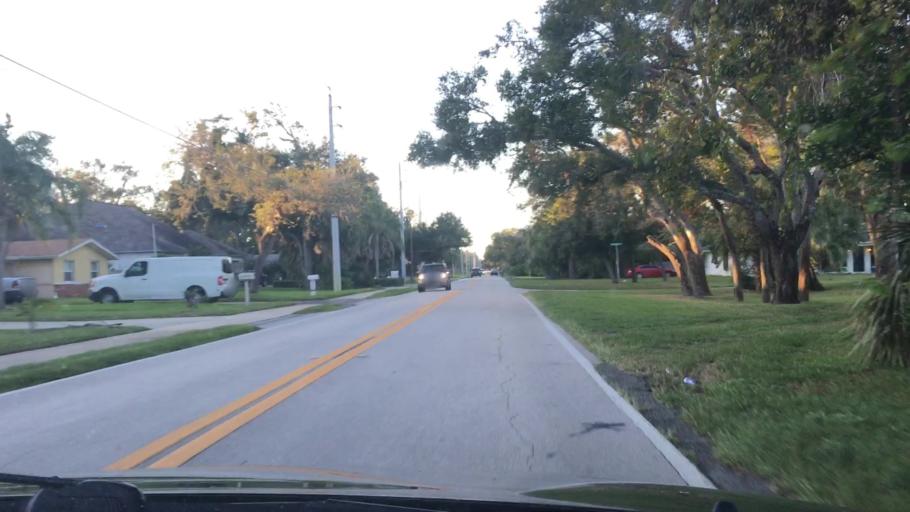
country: US
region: Florida
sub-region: Volusia County
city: Ormond Beach
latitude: 29.3113
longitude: -81.0684
